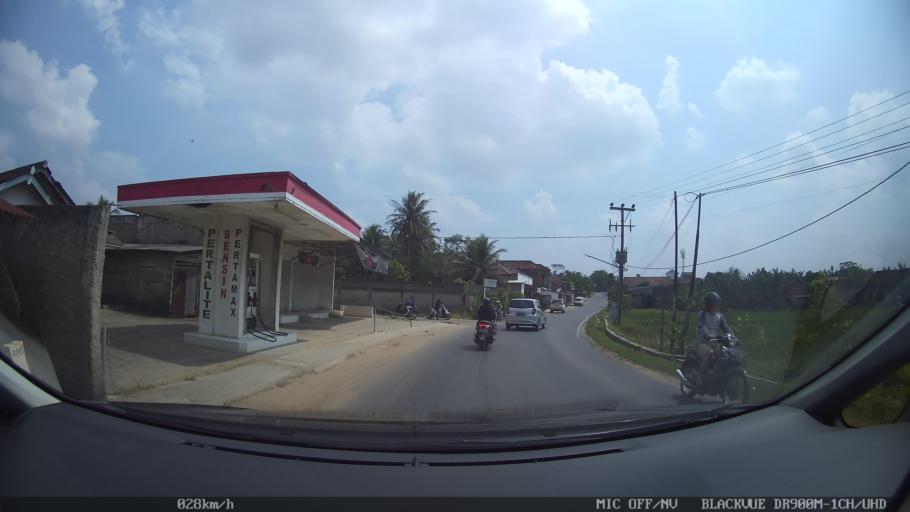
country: ID
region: Lampung
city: Pringsewu
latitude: -5.3702
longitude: 104.9661
